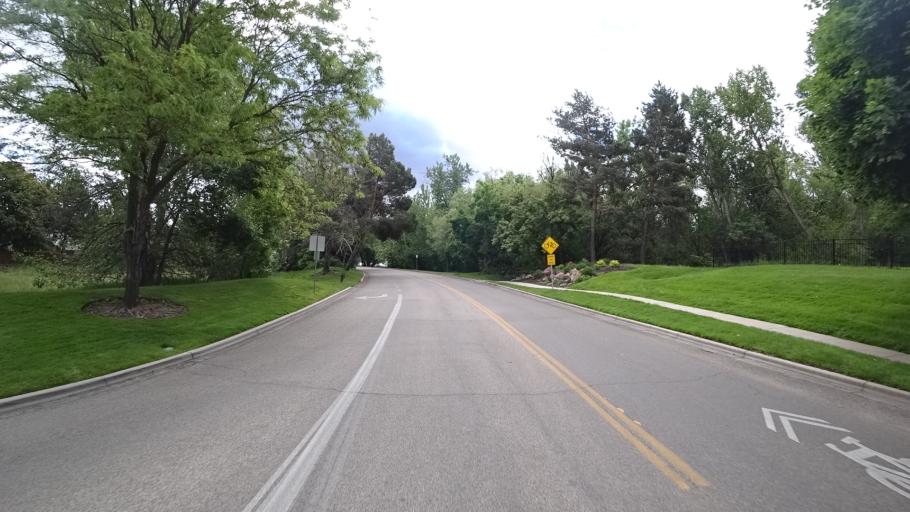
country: US
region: Idaho
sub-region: Ada County
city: Garden City
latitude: 43.6635
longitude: -116.2838
